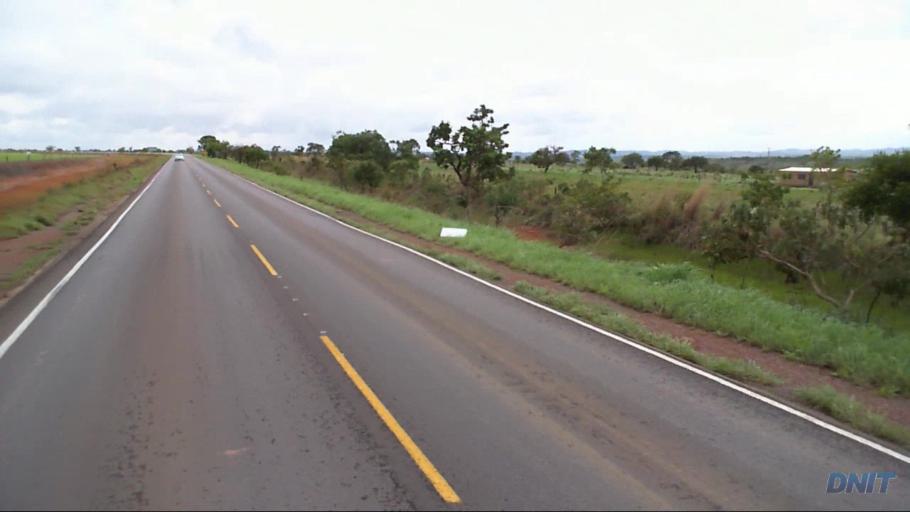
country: BR
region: Goias
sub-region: Padre Bernardo
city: Padre Bernardo
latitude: -15.3126
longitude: -48.2278
